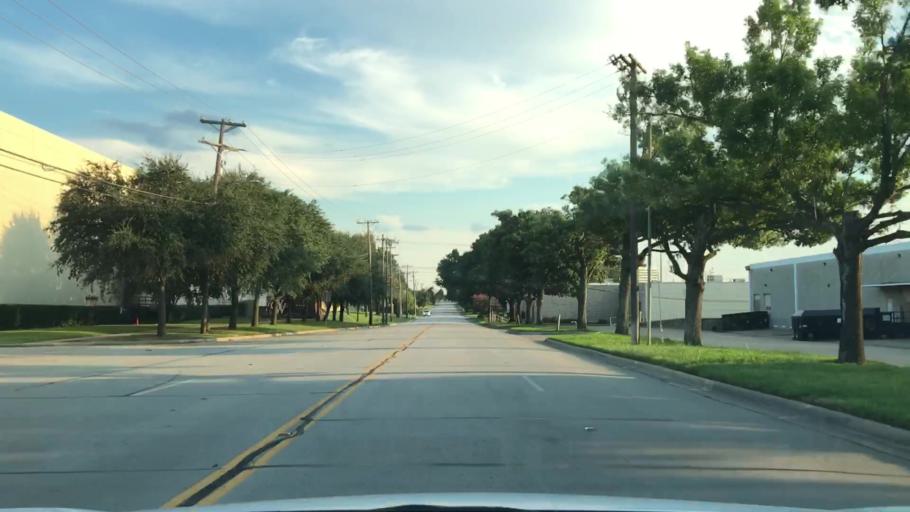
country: US
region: Texas
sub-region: Dallas County
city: Addison
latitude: 32.9391
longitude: -96.8306
